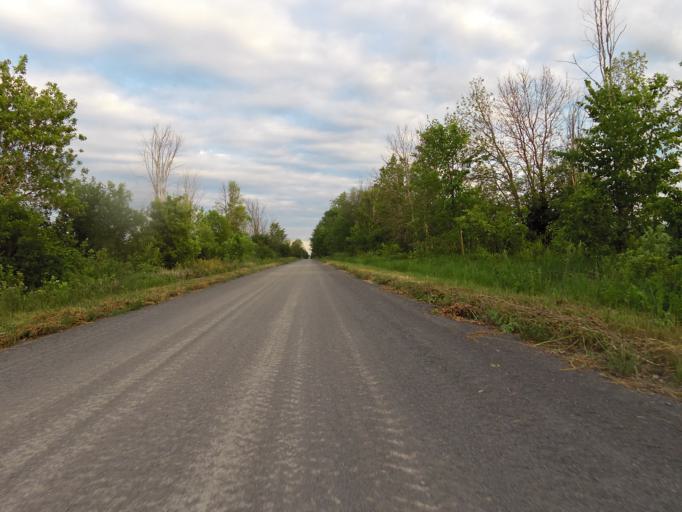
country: CA
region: Ontario
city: Arnprior
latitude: 45.3426
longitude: -76.2992
